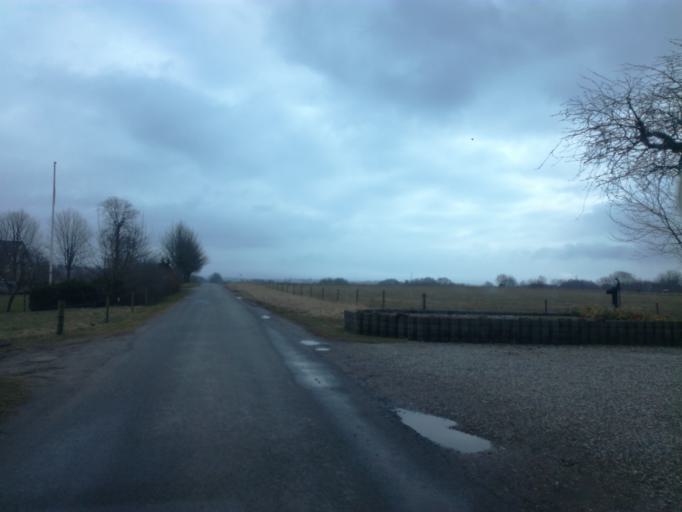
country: DK
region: South Denmark
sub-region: Vejle Kommune
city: Brejning
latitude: 55.6195
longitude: 9.6923
